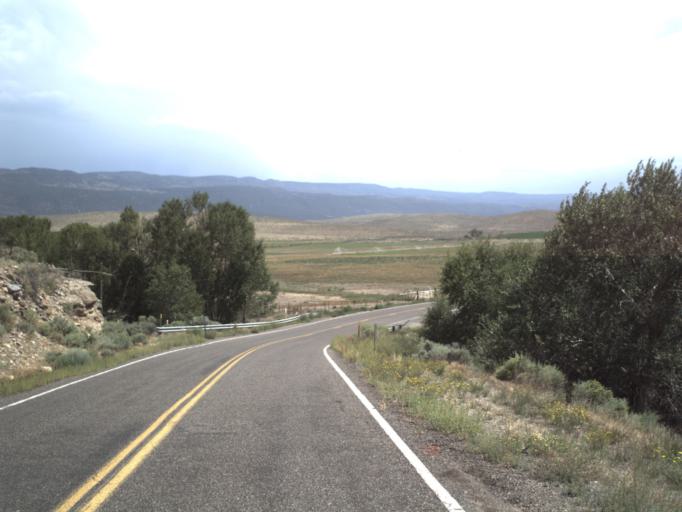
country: US
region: Utah
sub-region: Piute County
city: Junction
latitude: 38.0932
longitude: -111.9832
